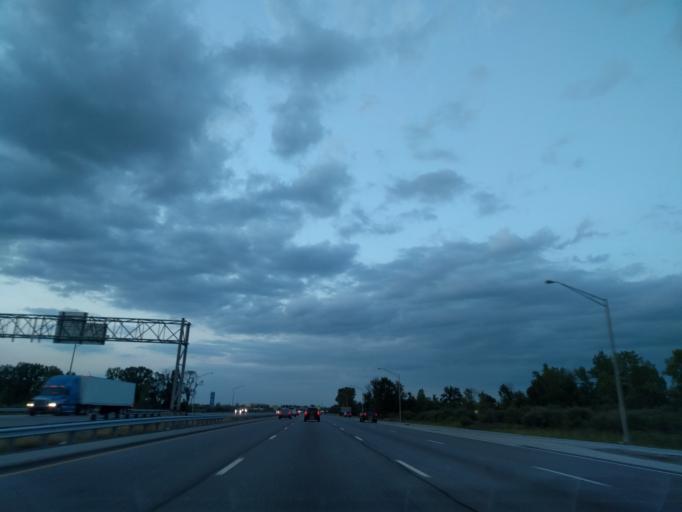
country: US
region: Indiana
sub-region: Johnson County
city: Greenwood
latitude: 39.6415
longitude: -86.0741
